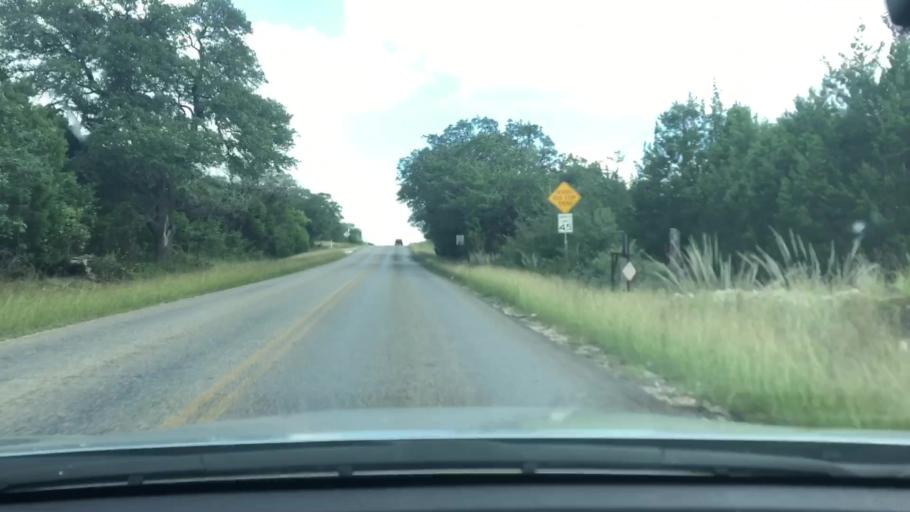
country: US
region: Texas
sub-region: Kendall County
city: Boerne
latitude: 29.7871
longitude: -98.6883
